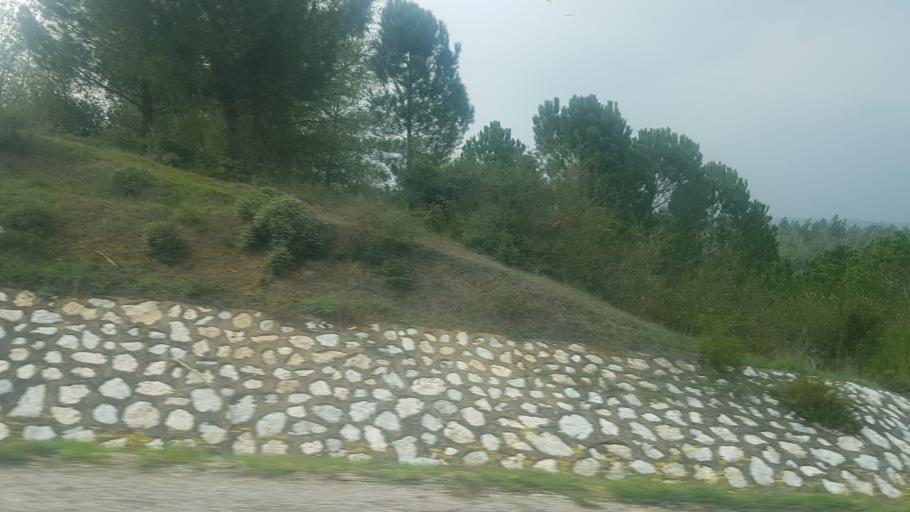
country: TR
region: Mersin
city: Yenice
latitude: 37.0766
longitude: 35.1708
